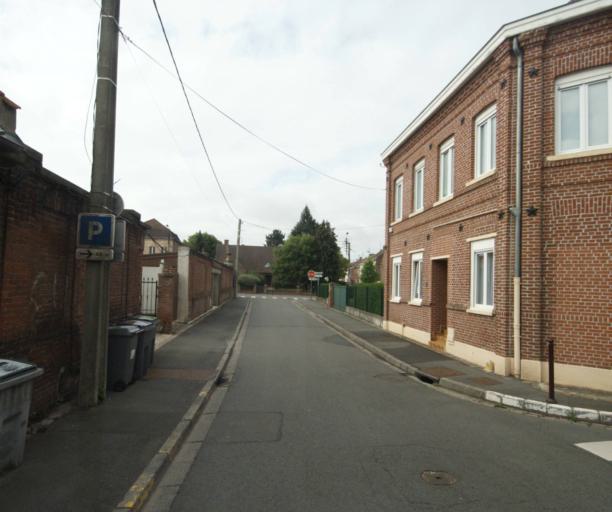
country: FR
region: Nord-Pas-de-Calais
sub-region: Departement du Nord
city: Ronchin
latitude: 50.5877
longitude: 3.1030
